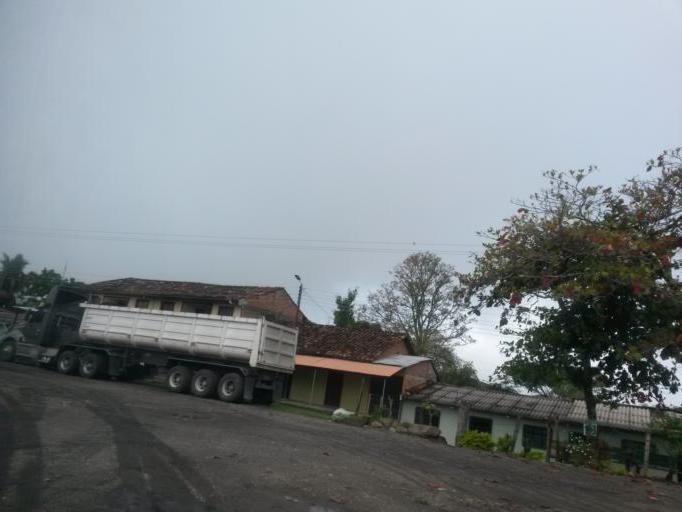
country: CO
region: Cauca
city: El Bordo
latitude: 2.1701
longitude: -76.9008
